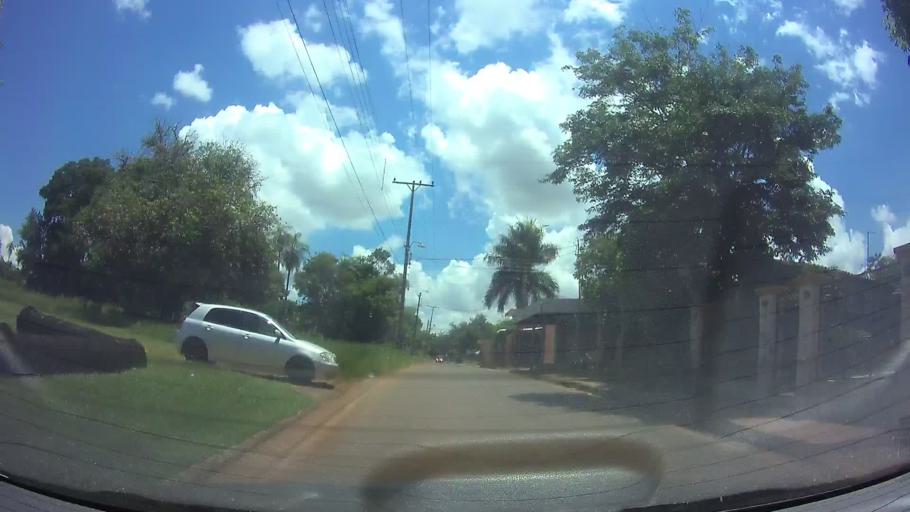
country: PY
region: Central
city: Itaugua
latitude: -25.3729
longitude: -57.3651
